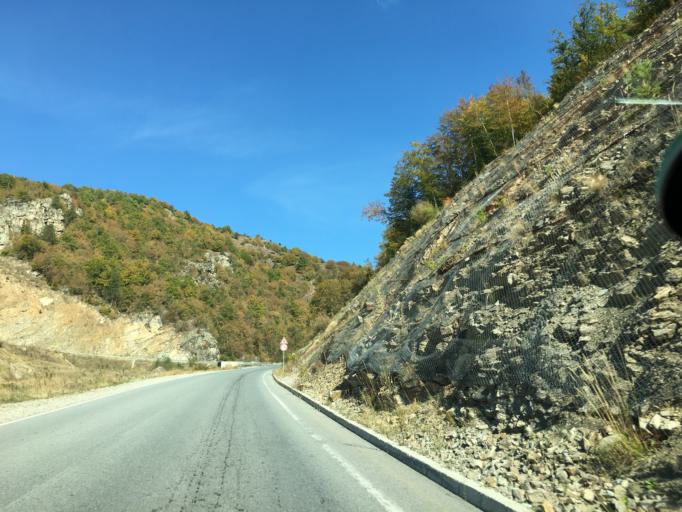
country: BG
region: Smolyan
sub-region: Obshtina Devin
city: Devin
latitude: 41.7586
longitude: 24.4396
